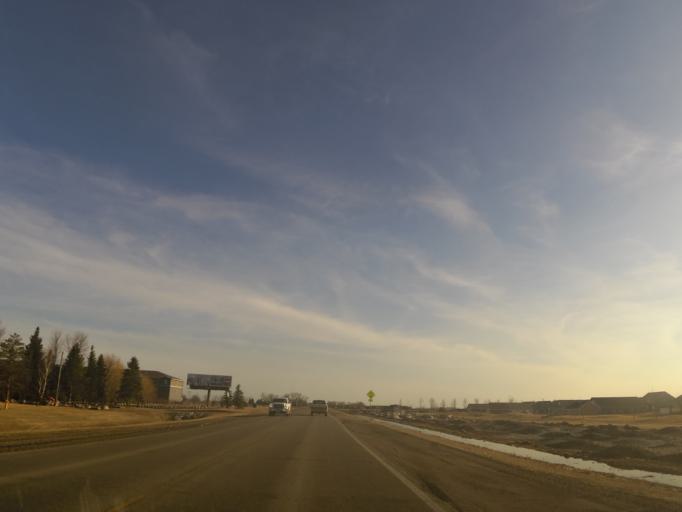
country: US
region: North Dakota
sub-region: Grand Forks County
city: Grand Forks
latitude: 47.8702
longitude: -97.0454
